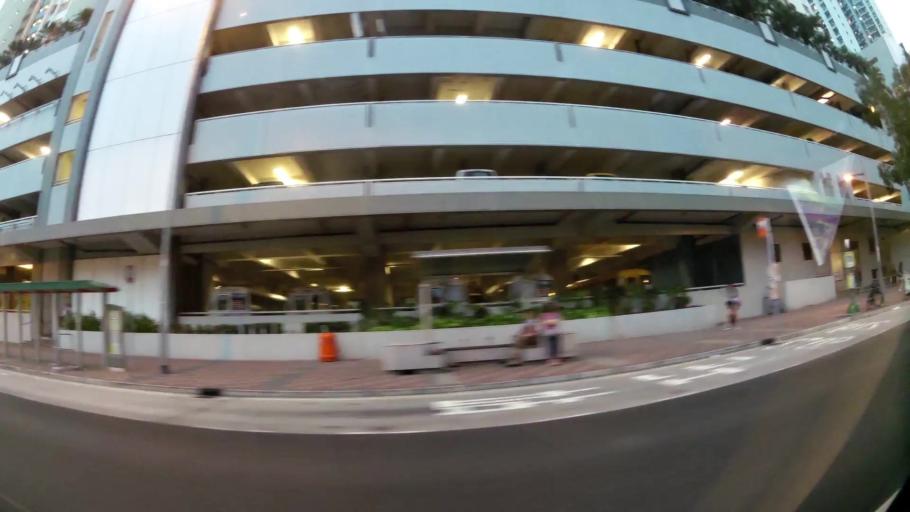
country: HK
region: Sham Shui Po
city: Sham Shui Po
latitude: 22.3283
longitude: 114.1538
